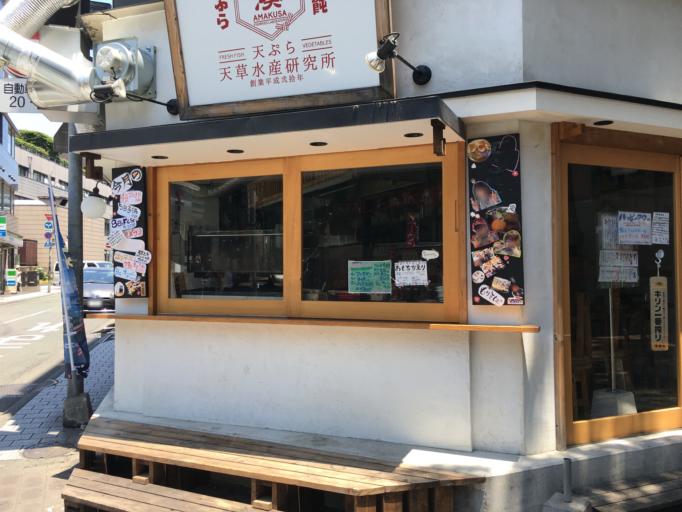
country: JP
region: Kumamoto
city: Kumamoto
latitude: 32.8023
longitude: 130.7077
